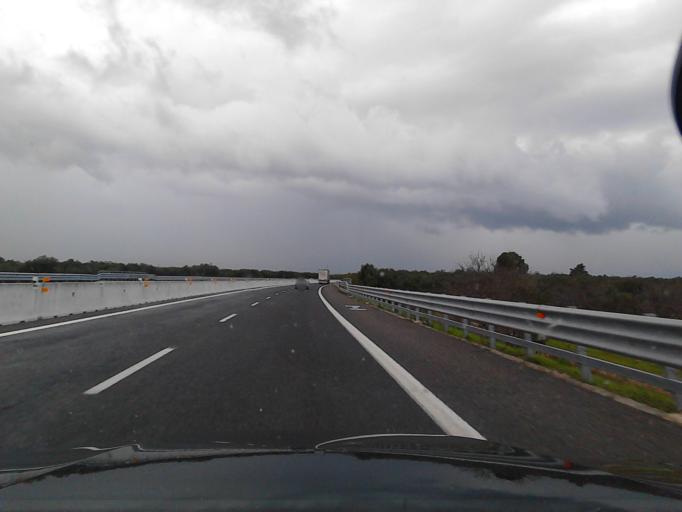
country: IT
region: Apulia
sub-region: Provincia di Bari
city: Modugno
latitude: 41.1027
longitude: 16.7495
